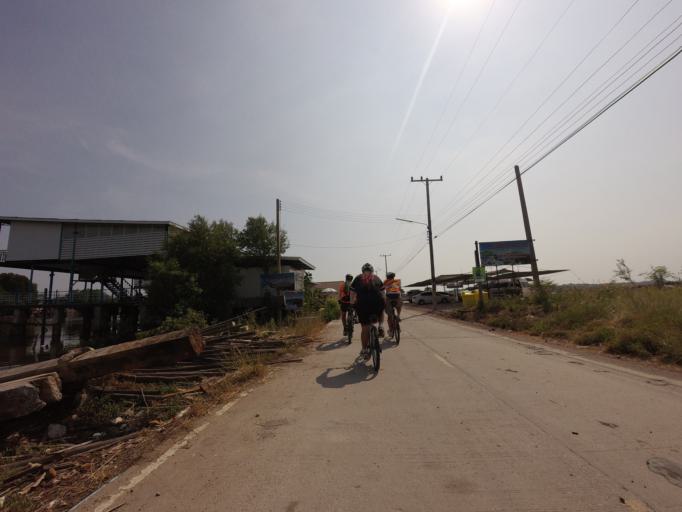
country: TH
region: Samut Sakhon
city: Samut Sakhon
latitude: 13.4991
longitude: 100.3862
